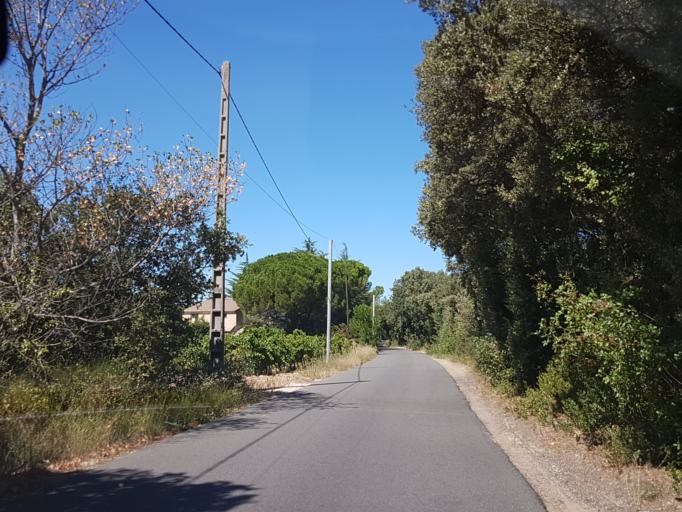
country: FR
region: Provence-Alpes-Cote d'Azur
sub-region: Departement du Vaucluse
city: Orange
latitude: 44.1167
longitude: 4.8098
